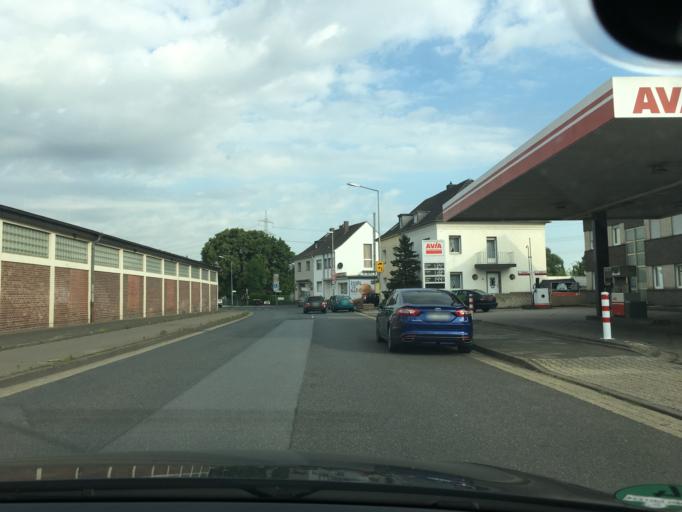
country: DE
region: North Rhine-Westphalia
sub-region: Regierungsbezirk Koln
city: Dueren
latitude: 50.8308
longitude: 6.4437
